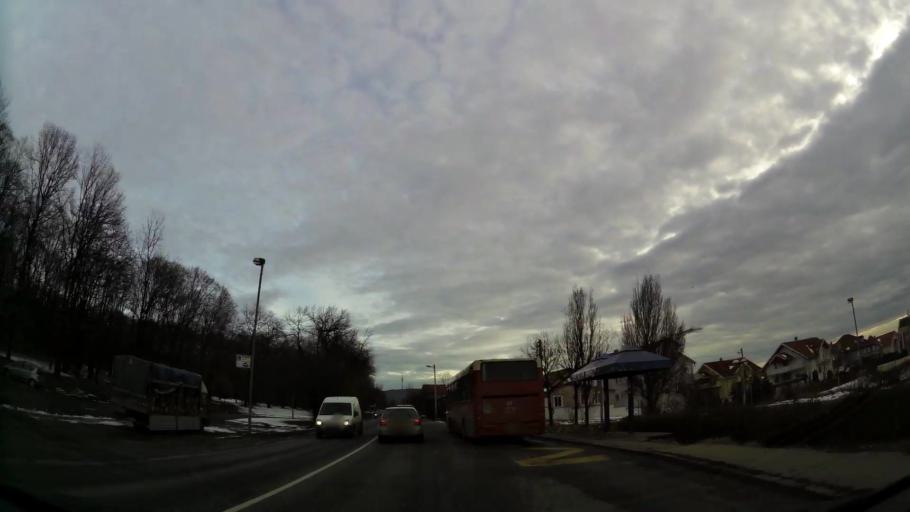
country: RS
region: Central Serbia
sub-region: Belgrade
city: Rakovica
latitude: 44.7306
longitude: 20.4832
